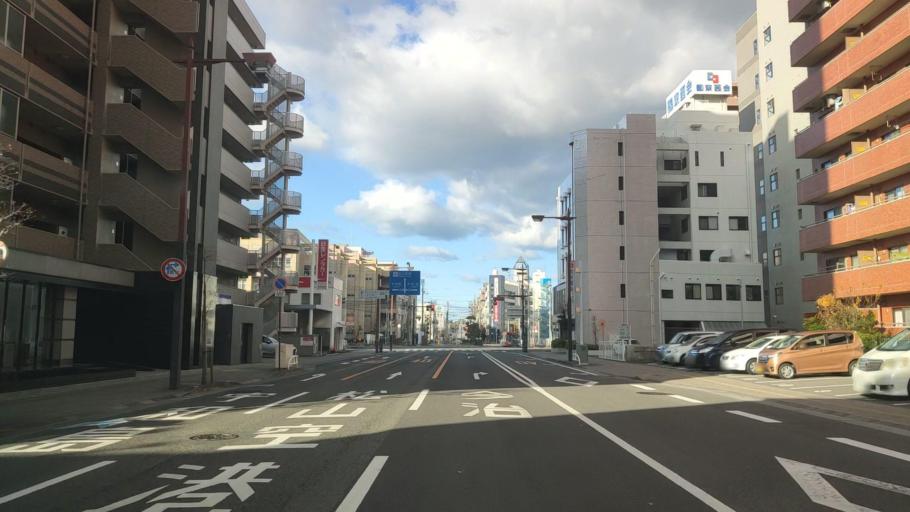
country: JP
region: Ehime
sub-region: Shikoku-chuo Shi
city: Matsuyama
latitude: 33.8369
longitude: 132.7597
